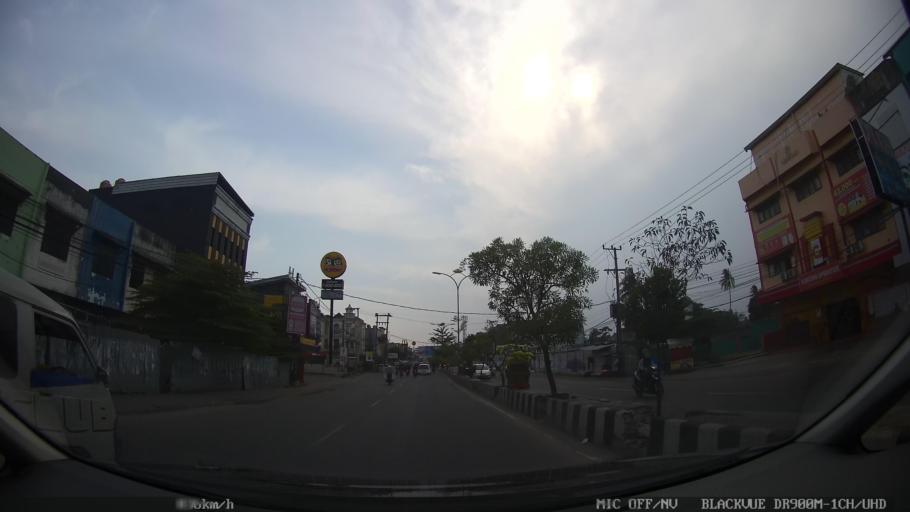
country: ID
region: Lampung
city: Bandarlampung
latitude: -5.4060
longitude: 105.2755
